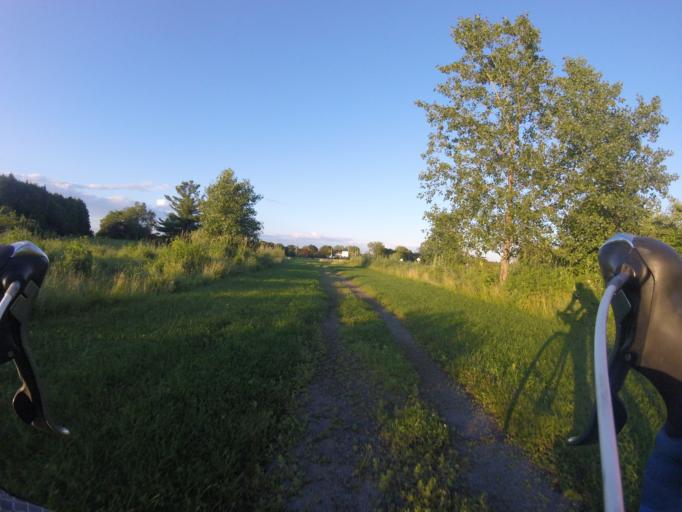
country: CA
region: Ontario
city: Bells Corners
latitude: 45.3539
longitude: -75.8527
